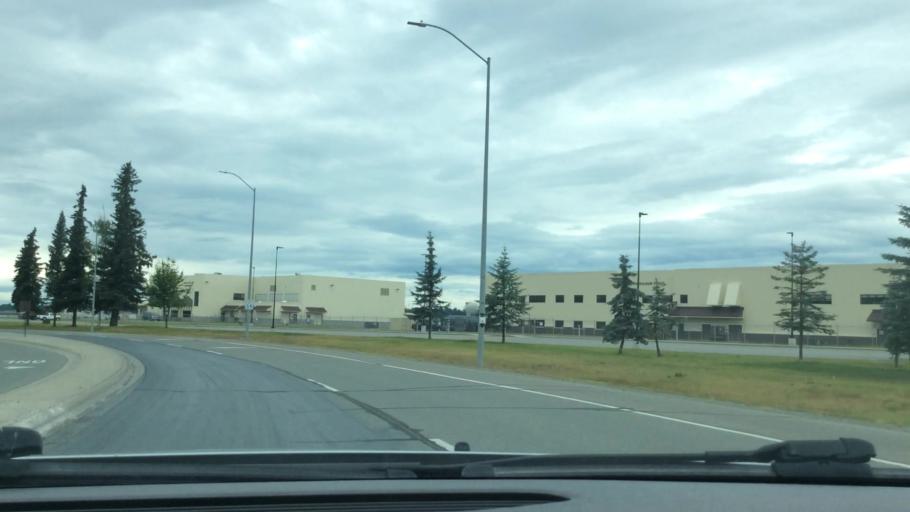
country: US
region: Alaska
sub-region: Anchorage Municipality
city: Anchorage
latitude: 61.2405
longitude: -149.7801
